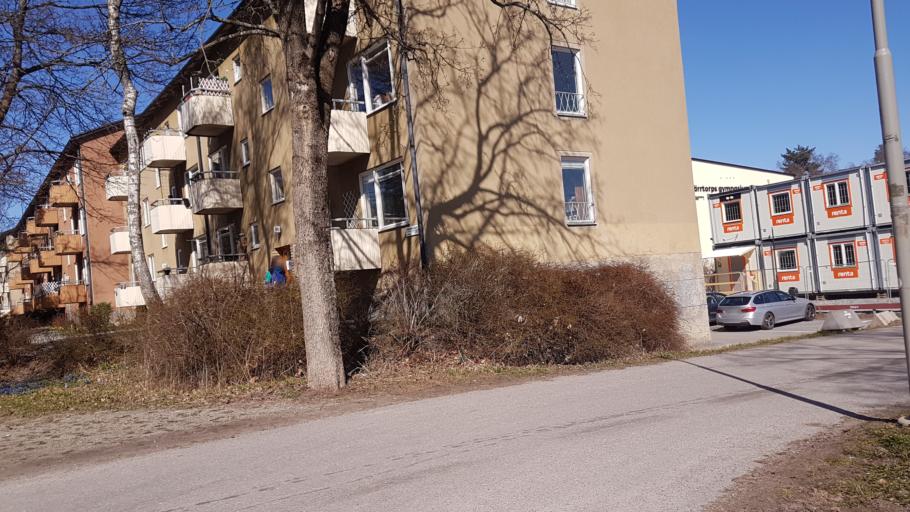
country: SE
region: Stockholm
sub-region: Nacka Kommun
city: Nacka
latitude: 59.2857
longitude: 18.1104
